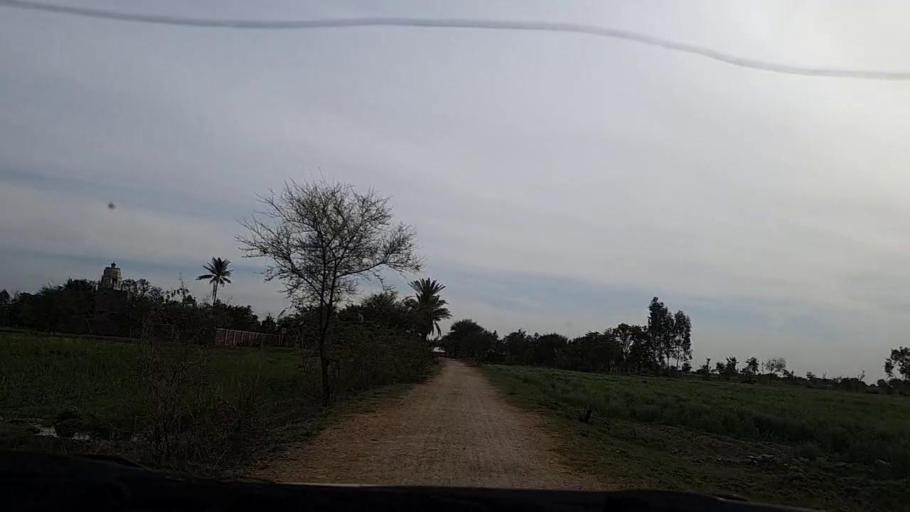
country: PK
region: Sindh
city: Dhoro Naro
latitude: 25.5134
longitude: 69.5158
